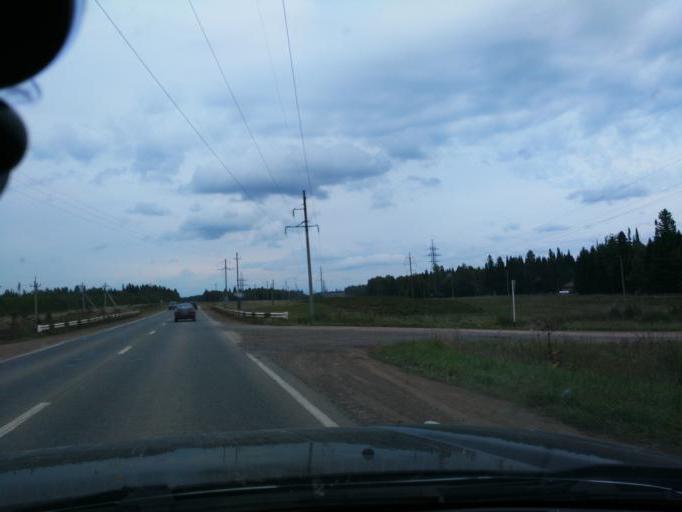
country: RU
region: Perm
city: Chernushka
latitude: 56.5297
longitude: 56.0401
